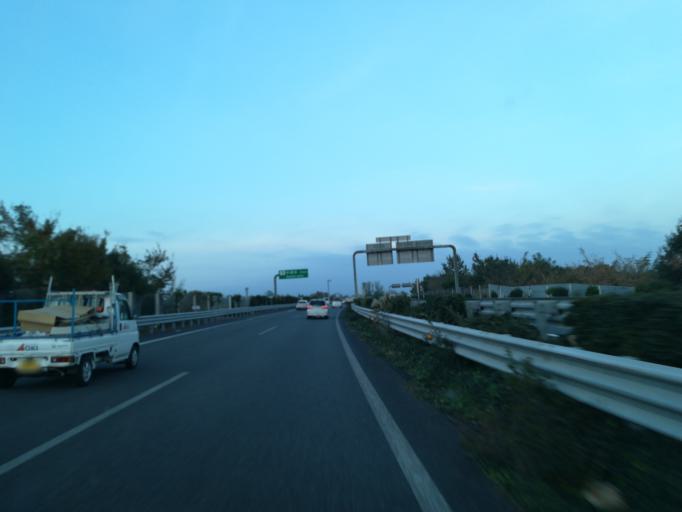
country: JP
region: Gunma
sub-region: Sawa-gun
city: Tamamura
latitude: 36.3268
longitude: 139.0774
